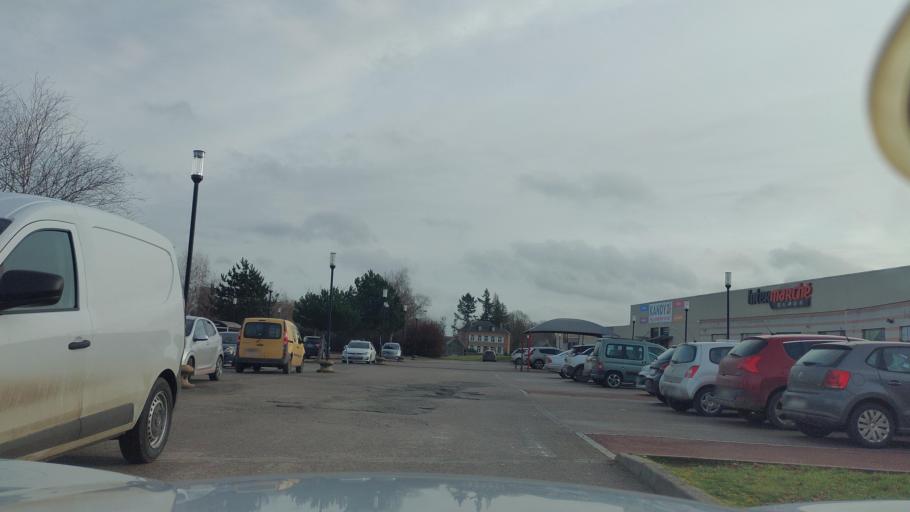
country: FR
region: Picardie
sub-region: Departement de la Somme
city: Oisemont
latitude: 49.9593
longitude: 1.7663
